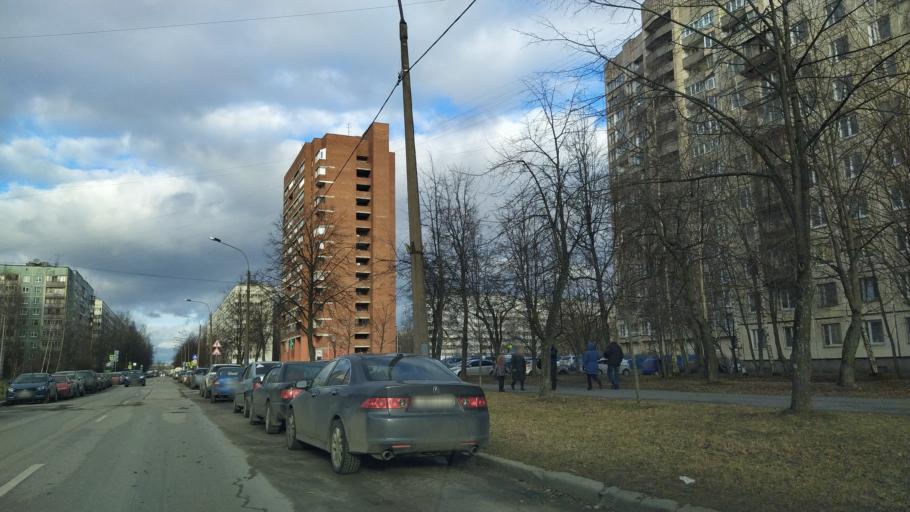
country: RU
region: Leningrad
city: Parnas
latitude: 60.0489
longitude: 30.3684
